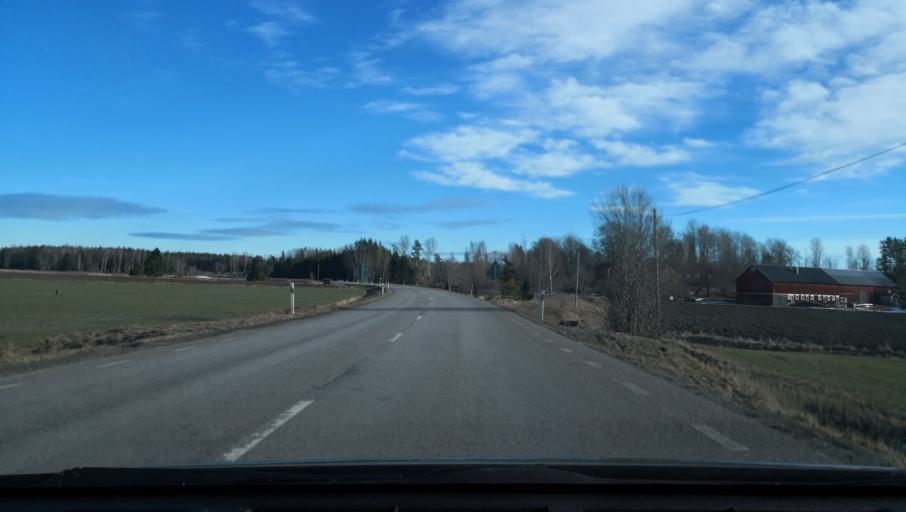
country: SE
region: Uppsala
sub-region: Osthammars Kommun
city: Osterbybruk
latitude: 60.1633
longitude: 17.9816
